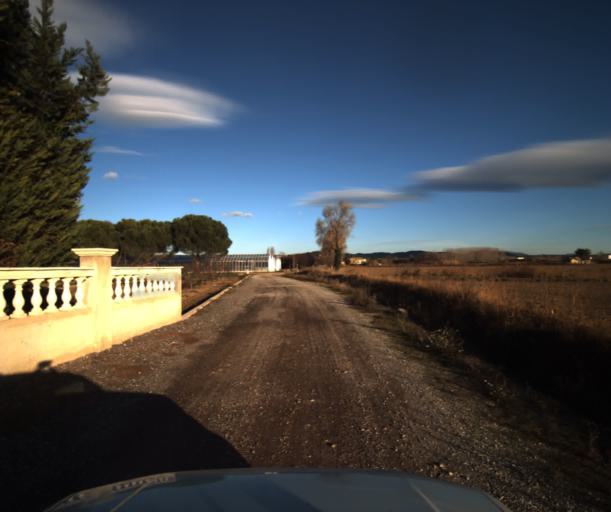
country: FR
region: Provence-Alpes-Cote d'Azur
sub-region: Departement du Vaucluse
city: Pertuis
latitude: 43.6830
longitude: 5.4865
